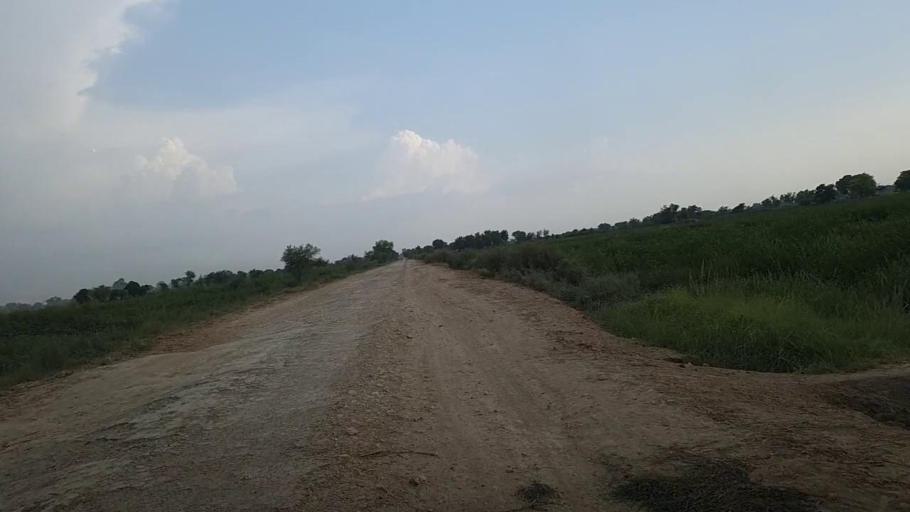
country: PK
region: Sindh
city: Khanpur
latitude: 27.8619
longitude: 69.4871
